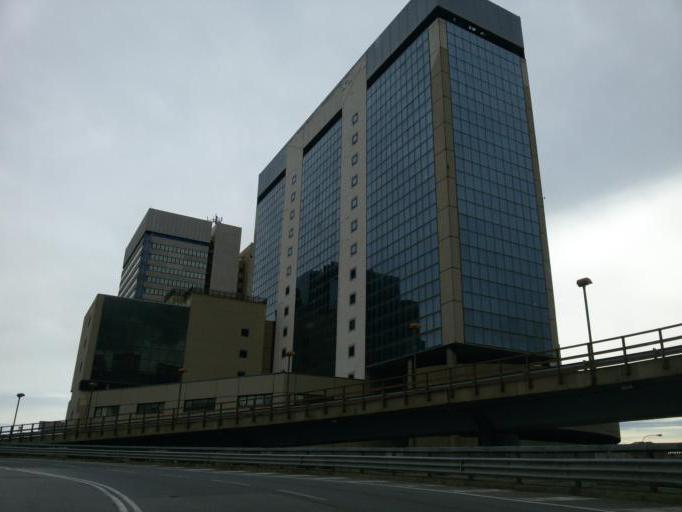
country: IT
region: Liguria
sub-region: Provincia di Genova
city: San Teodoro
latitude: 44.4093
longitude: 8.9026
